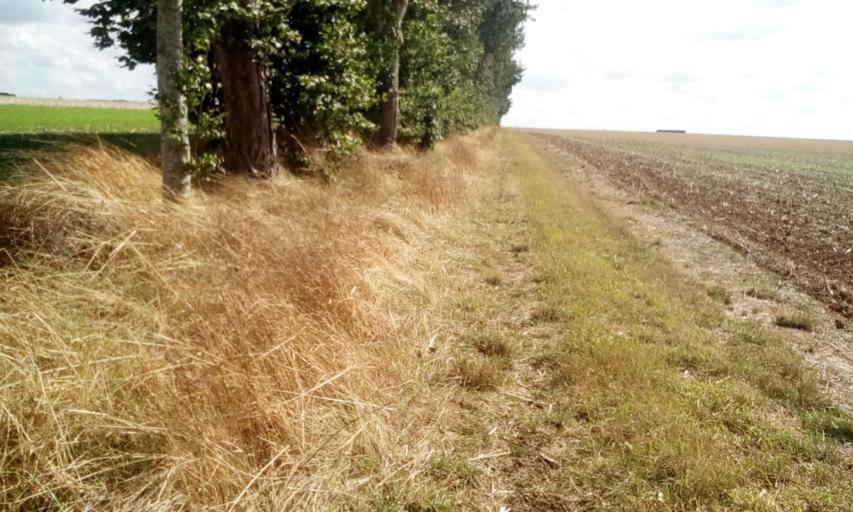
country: FR
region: Lower Normandy
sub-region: Departement du Calvados
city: Saint-Sylvain
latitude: 49.0841
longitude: -0.1974
